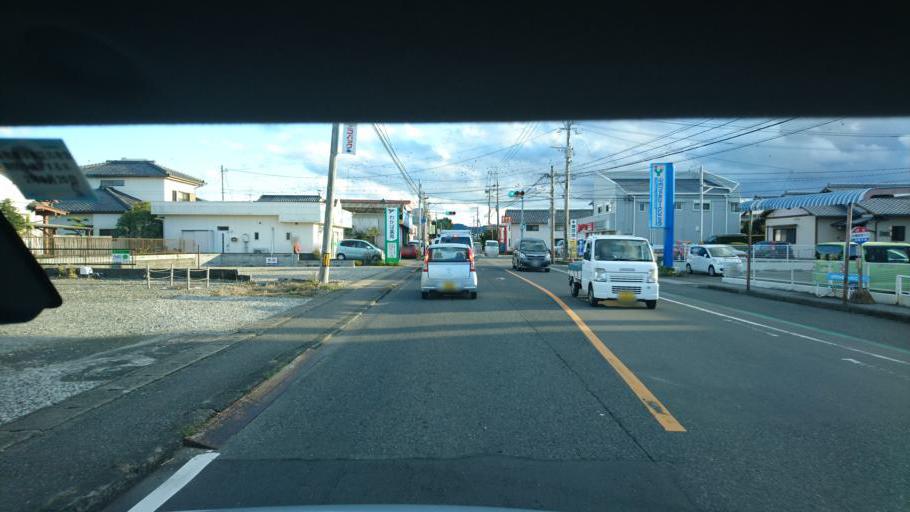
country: JP
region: Miyazaki
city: Miyazaki-shi
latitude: 31.8662
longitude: 131.4320
